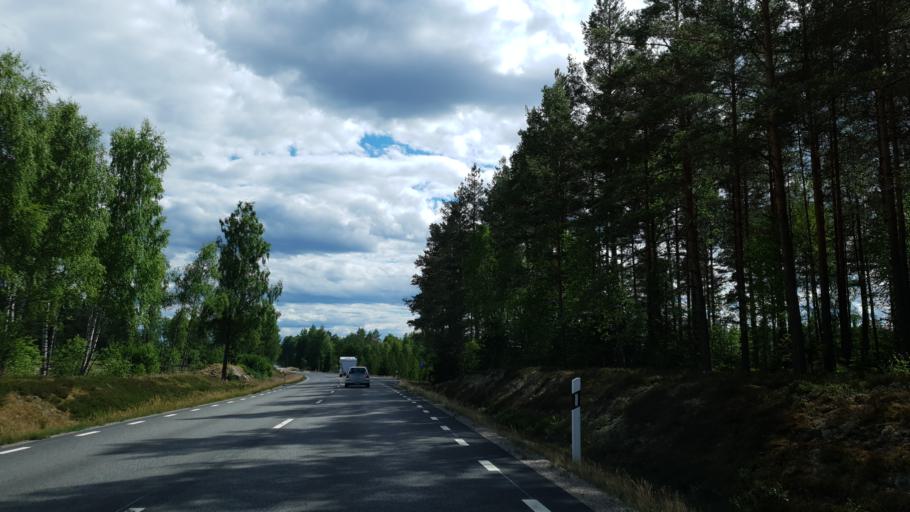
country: SE
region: Kronoberg
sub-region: Lessebo Kommun
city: Lessebo
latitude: 56.7987
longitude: 15.4121
